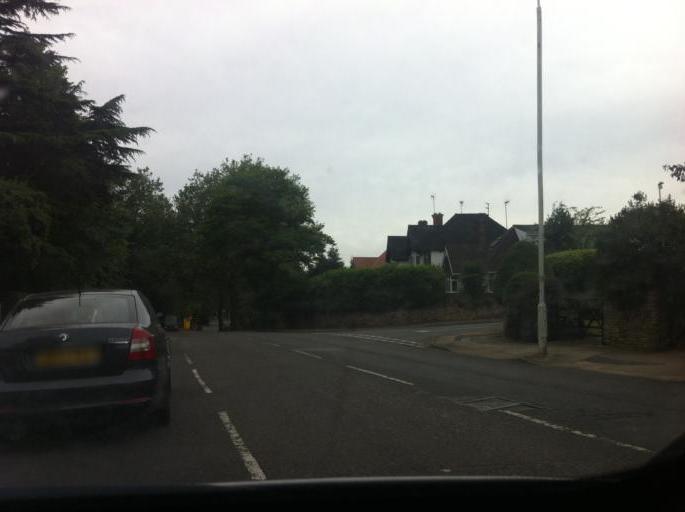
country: GB
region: England
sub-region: Northamptonshire
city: Northampton
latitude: 52.2510
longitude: -0.8543
